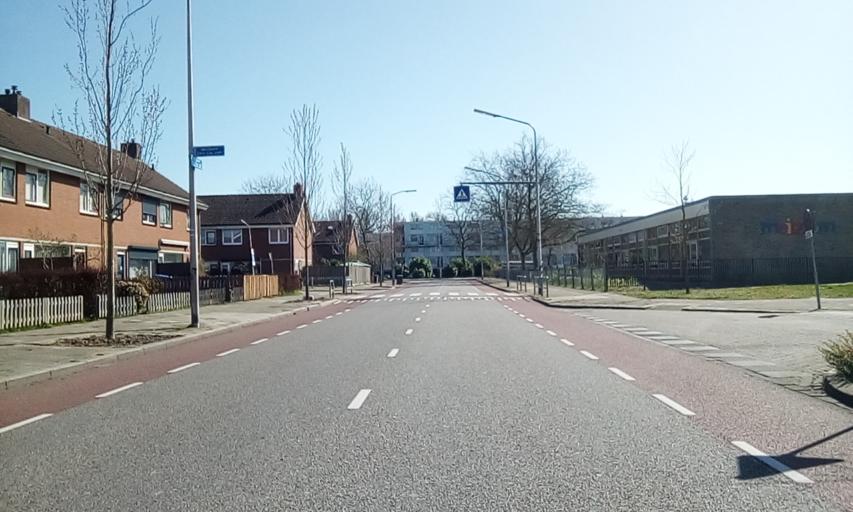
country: NL
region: Gelderland
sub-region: Gemeente Nijmegen
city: Lindenholt
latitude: 51.8114
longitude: 5.7950
